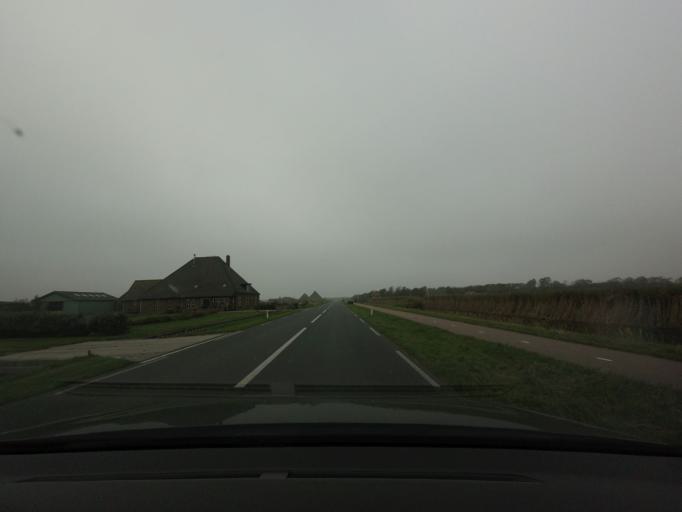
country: NL
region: North Holland
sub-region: Gemeente Schagen
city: Harenkarspel
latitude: 52.7575
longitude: 4.6696
